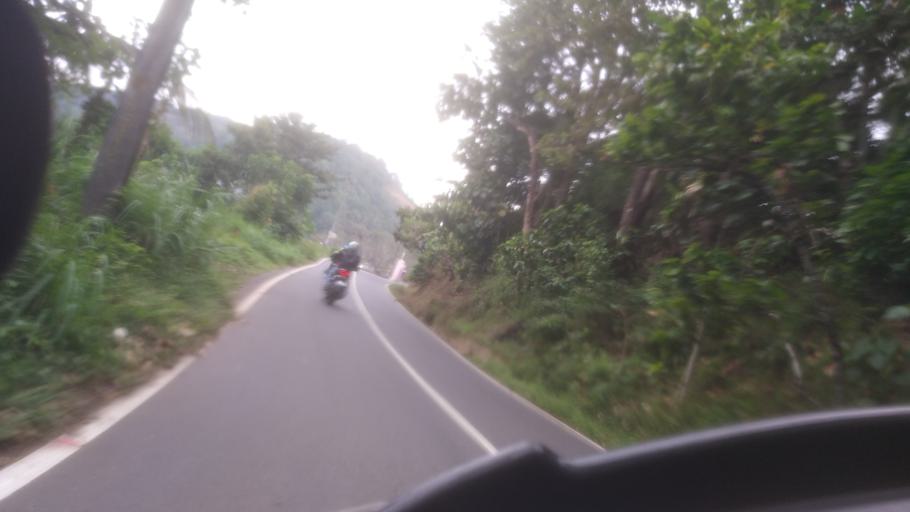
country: IN
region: Kerala
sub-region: Idukki
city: Idukki
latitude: 9.9562
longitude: 77.0103
